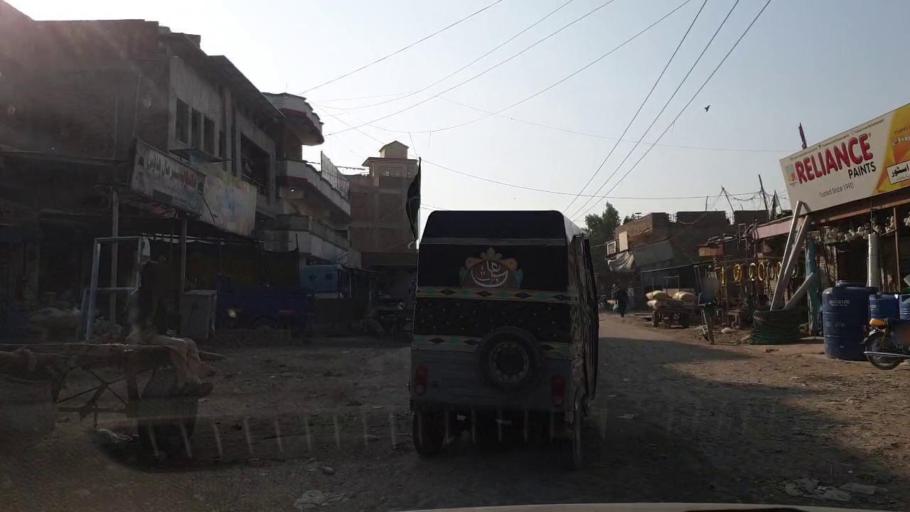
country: PK
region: Sindh
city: Kotri
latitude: 25.3592
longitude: 68.2751
